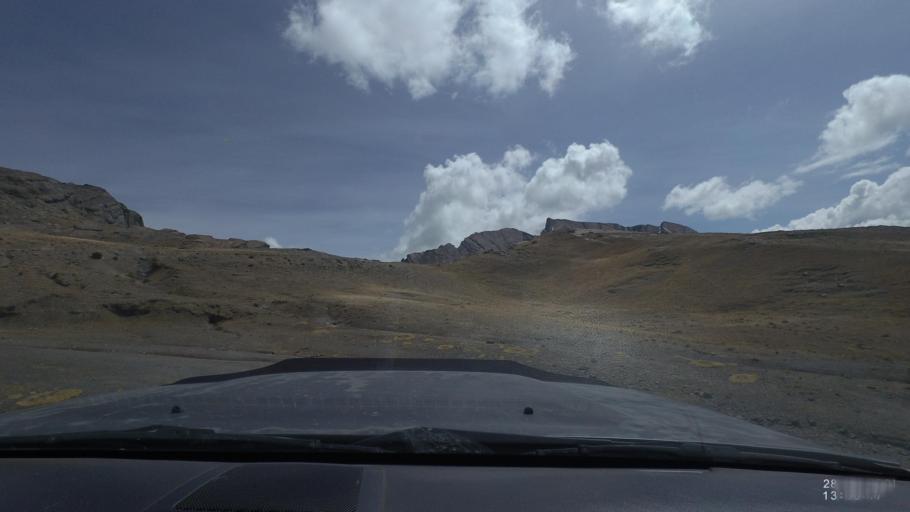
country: BO
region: Cochabamba
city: Sipe Sipe
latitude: -17.2757
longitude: -66.3831
